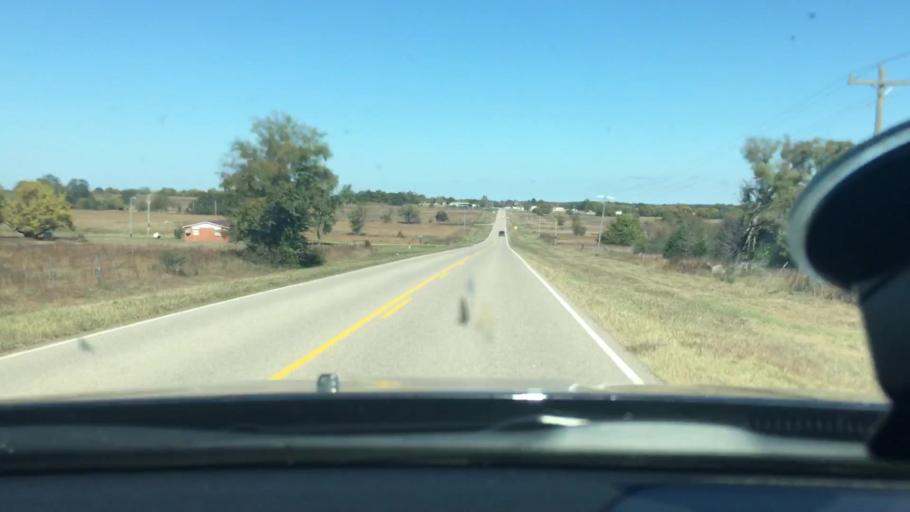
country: US
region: Oklahoma
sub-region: Johnston County
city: Tishomingo
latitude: 34.4325
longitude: -96.6360
